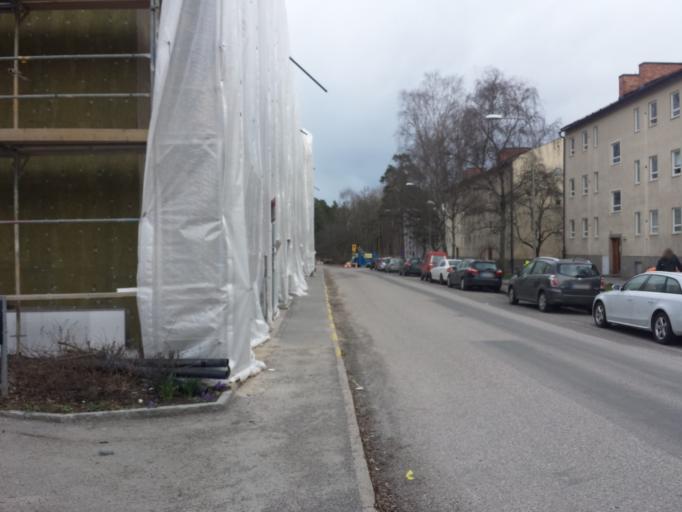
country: SE
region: Stockholm
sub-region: Nacka Kommun
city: Nacka
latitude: 59.2898
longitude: 18.1201
